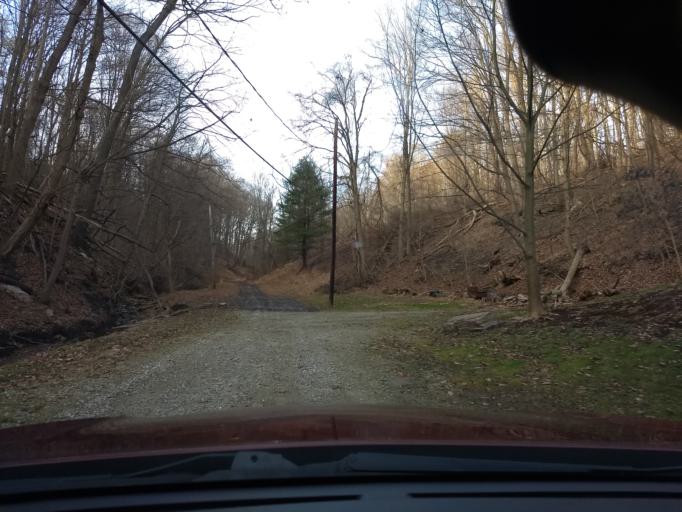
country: US
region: Pennsylvania
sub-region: Allegheny County
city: Brentwood
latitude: 40.3721
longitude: -79.9642
